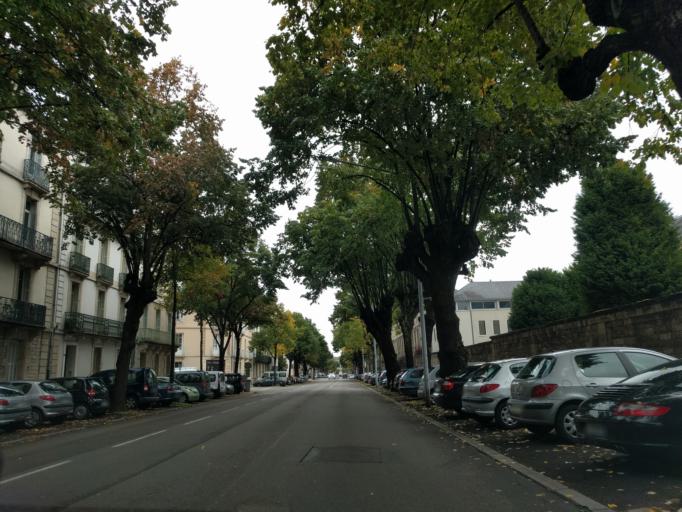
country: FR
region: Bourgogne
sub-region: Departement de la Cote-d'Or
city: Dijon
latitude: 47.3249
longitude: 5.0477
